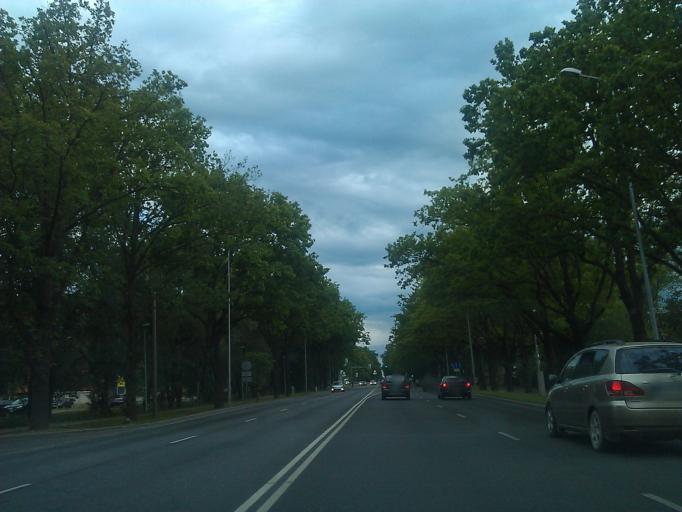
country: LV
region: Marupe
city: Marupe
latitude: 56.9016
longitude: 24.0800
